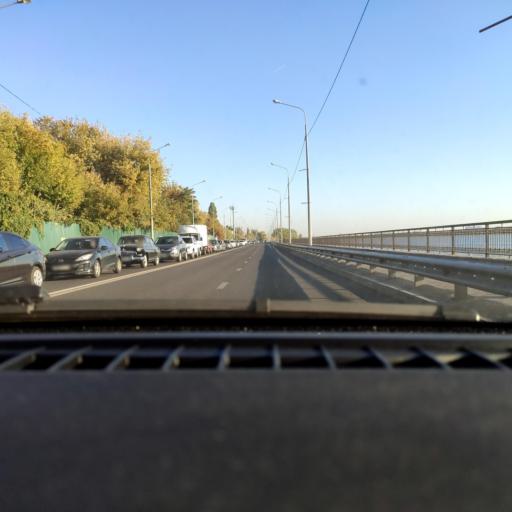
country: RU
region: Voronezj
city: Voronezh
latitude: 51.6708
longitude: 39.2234
